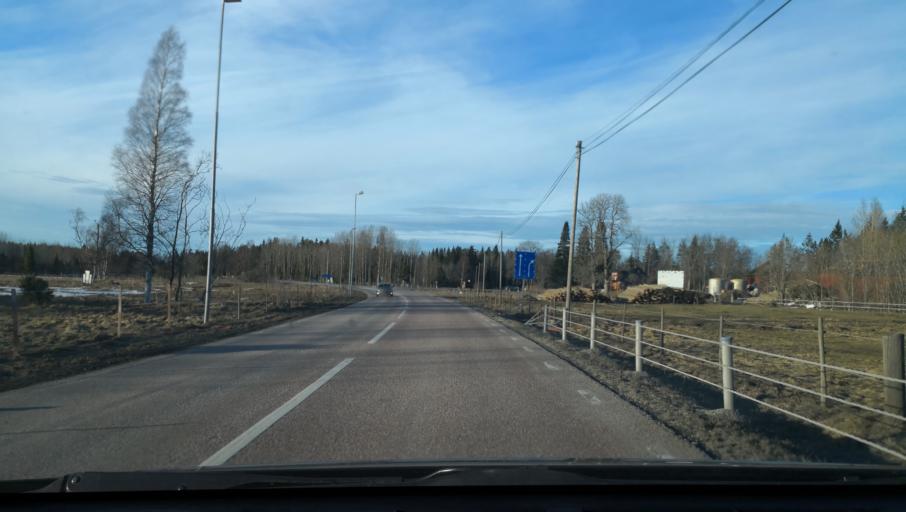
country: SE
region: Uppsala
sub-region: Osthammars Kommun
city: OEsthammar
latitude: 60.2961
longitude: 18.2841
